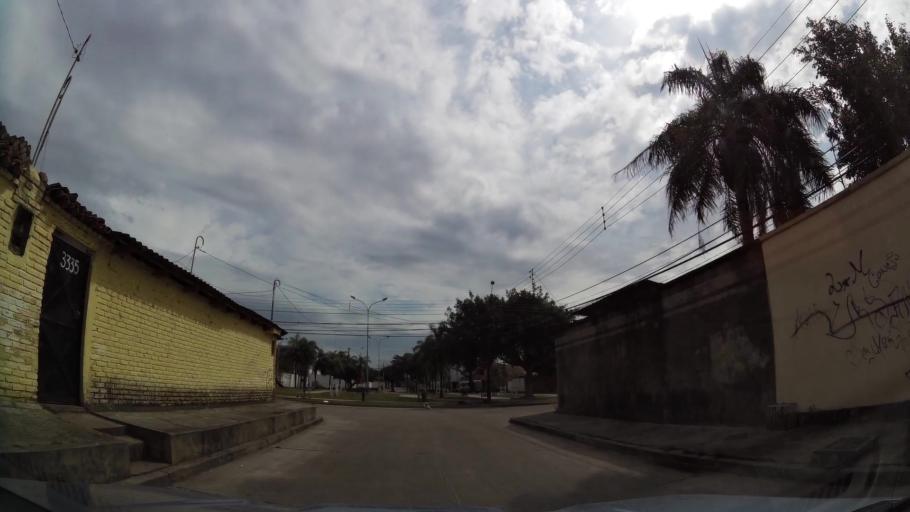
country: BO
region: Santa Cruz
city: Santa Cruz de la Sierra
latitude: -17.7789
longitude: -63.2089
